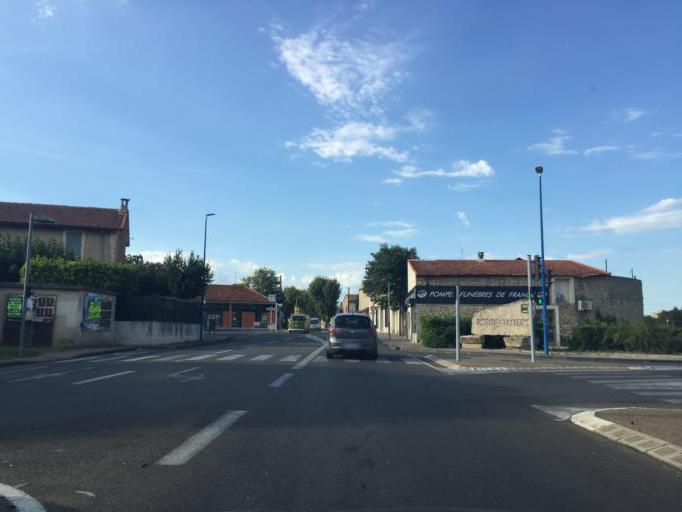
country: FR
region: Provence-Alpes-Cote d'Azur
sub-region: Departement du Vaucluse
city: Carpentras
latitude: 44.0442
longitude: 5.0485
